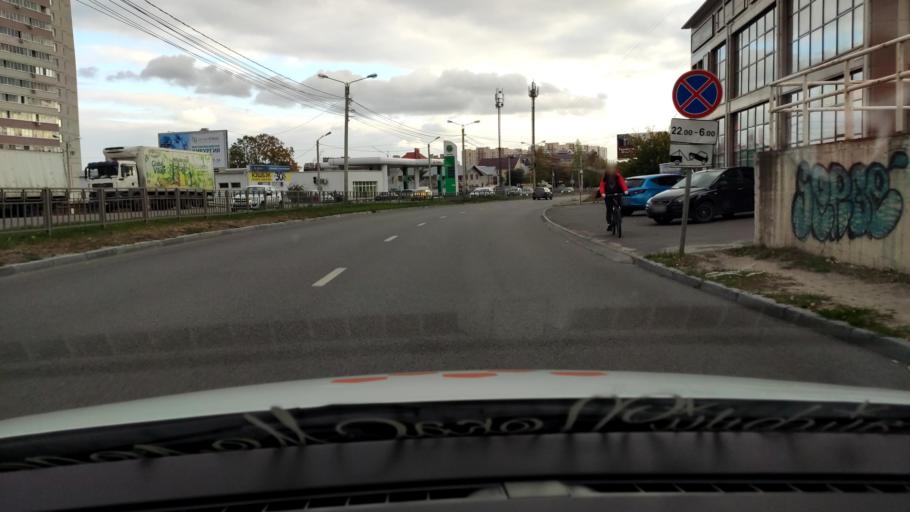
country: RU
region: Voronezj
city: Voronezh
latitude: 51.7126
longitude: 39.1943
